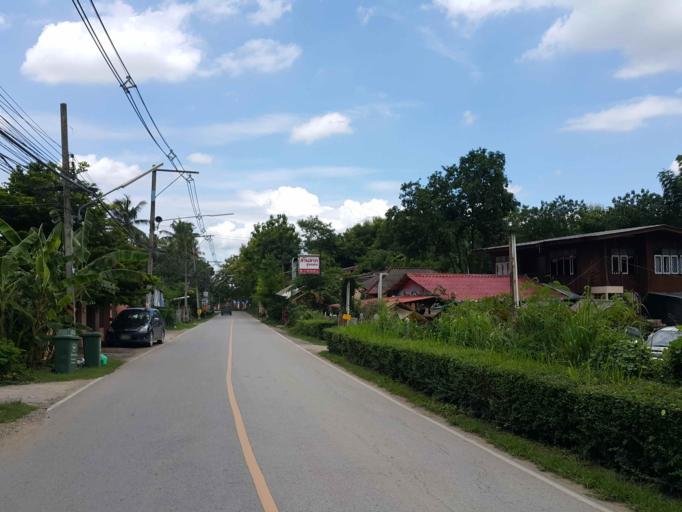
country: TH
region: Chiang Mai
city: Chiang Mai
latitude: 18.8474
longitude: 98.9871
